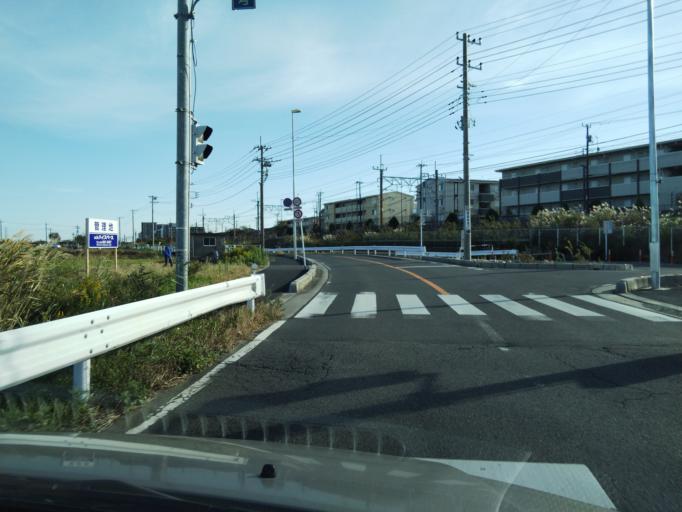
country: JP
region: Saitama
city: Yoshikawa
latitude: 35.8748
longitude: 139.8493
